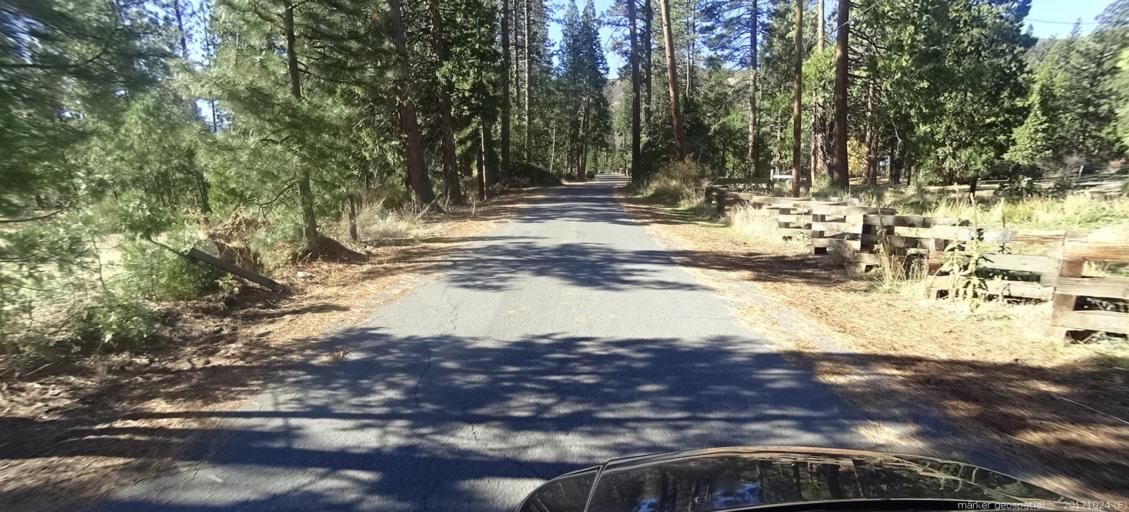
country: US
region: California
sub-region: Shasta County
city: Burney
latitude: 40.8122
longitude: -121.5056
